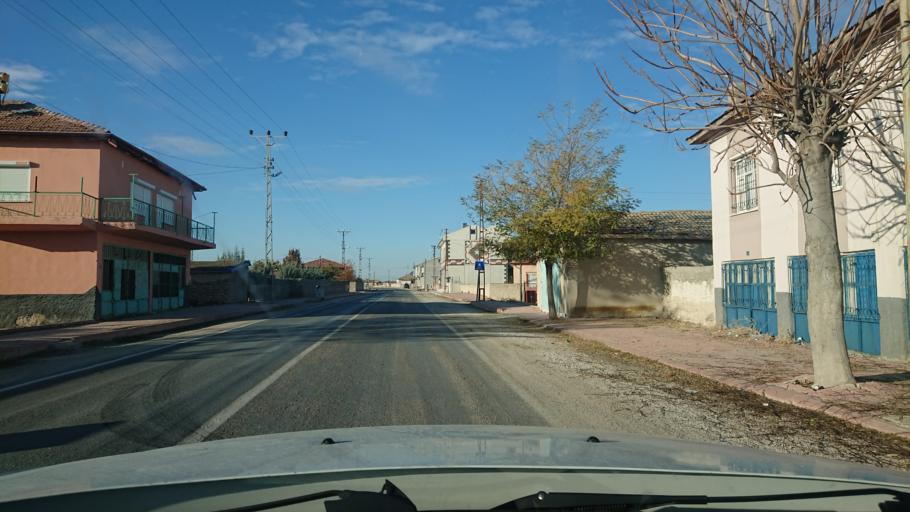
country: TR
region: Aksaray
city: Eskil
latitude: 38.5629
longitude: 33.1948
